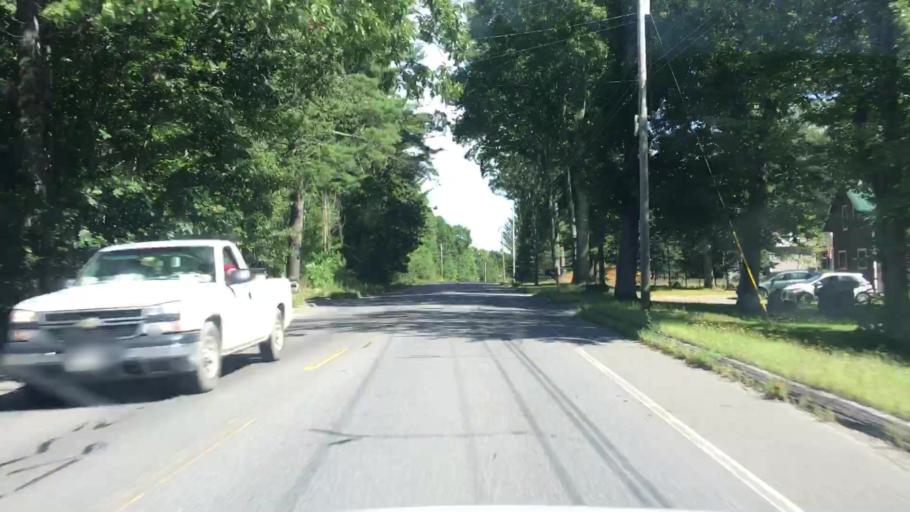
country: US
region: Maine
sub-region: Penobscot County
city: Garland
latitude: 45.0846
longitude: -69.2270
